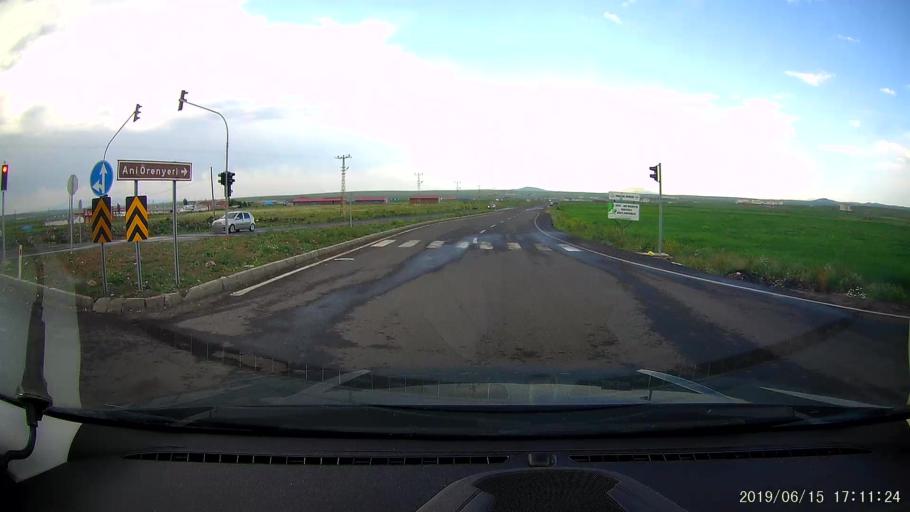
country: TR
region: Kars
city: Kars
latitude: 40.6135
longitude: 43.1333
